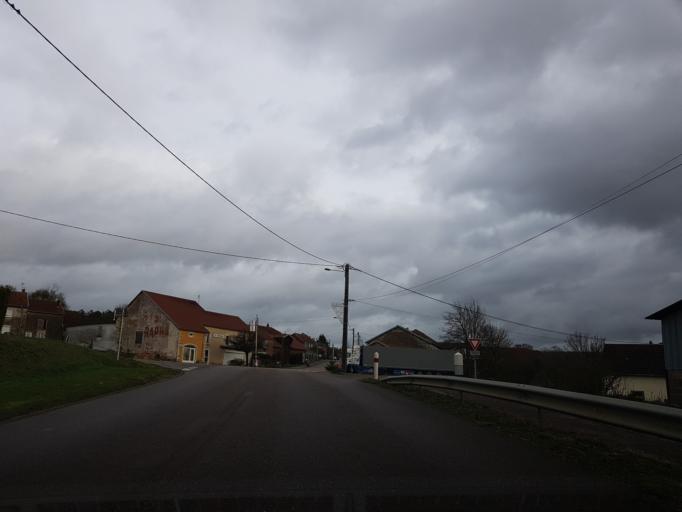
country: FR
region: Franche-Comte
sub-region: Departement de la Haute-Saone
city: Jussey
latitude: 47.7209
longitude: 5.8421
